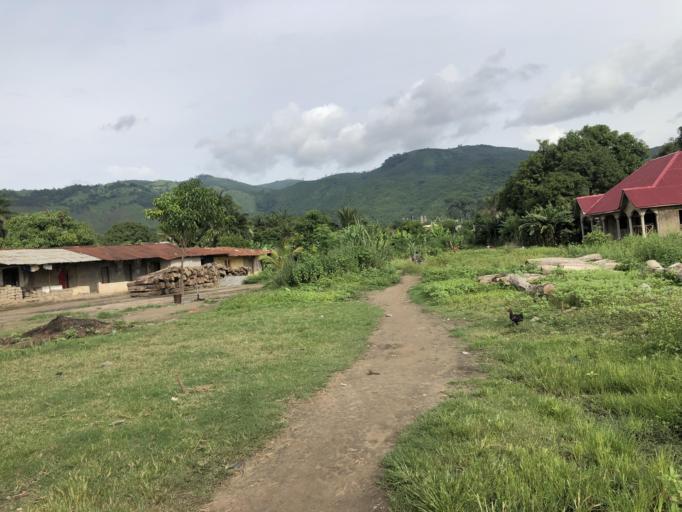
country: SL
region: Northern Province
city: Bumbuna
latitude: 9.0471
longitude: -11.7491
